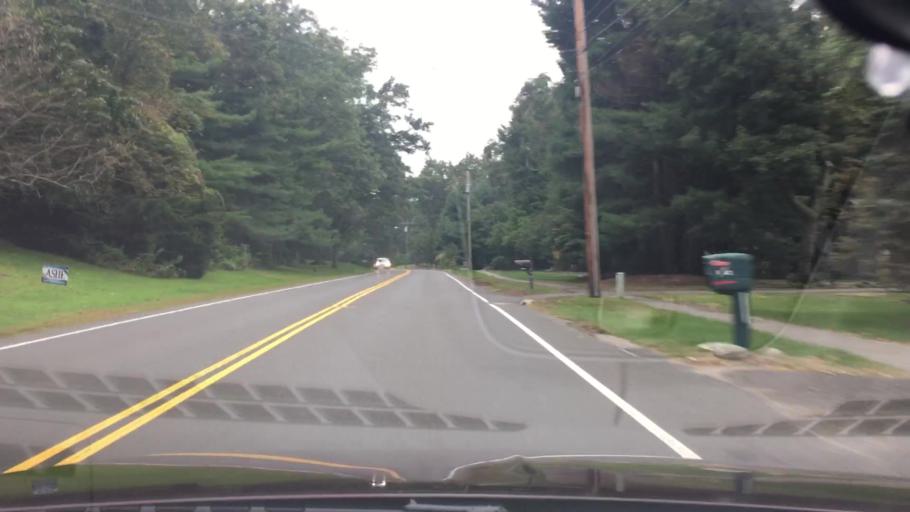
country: US
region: Connecticut
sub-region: Hartford County
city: Sherwood Manor
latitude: 42.0384
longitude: -72.5408
